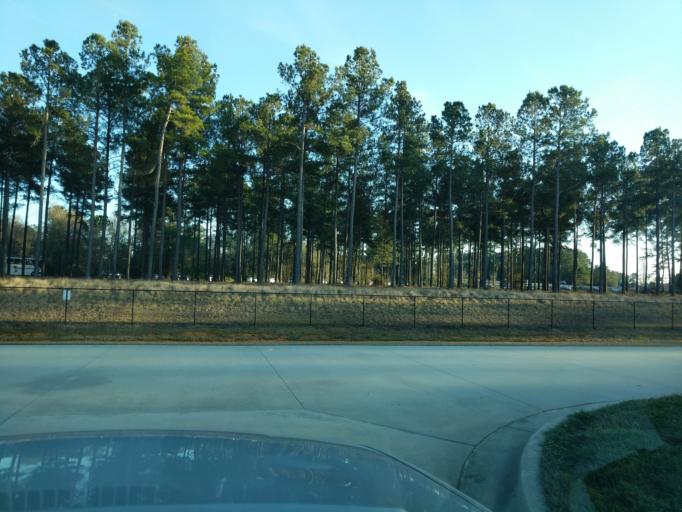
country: US
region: South Carolina
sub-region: Orangeburg County
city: Brookdale
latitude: 33.5239
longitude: -80.7929
